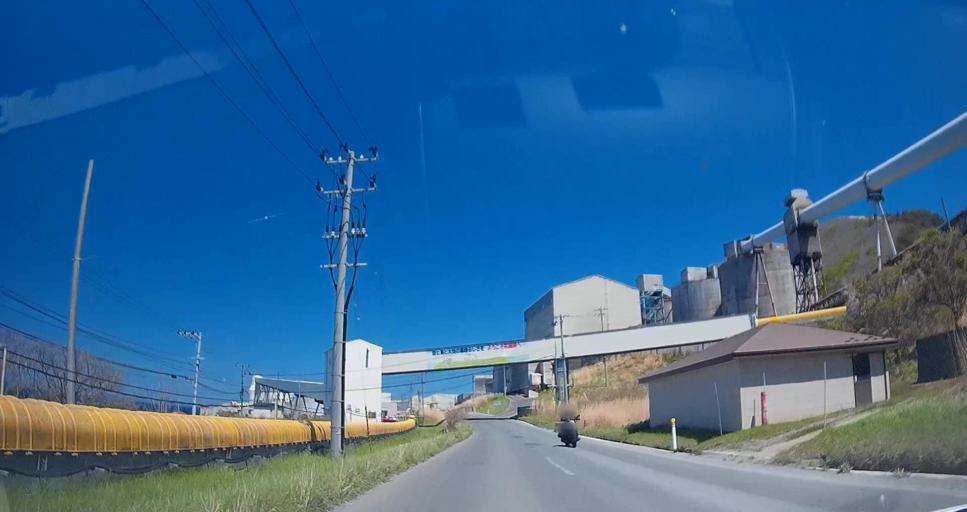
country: JP
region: Aomori
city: Mutsu
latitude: 41.4084
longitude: 141.4374
